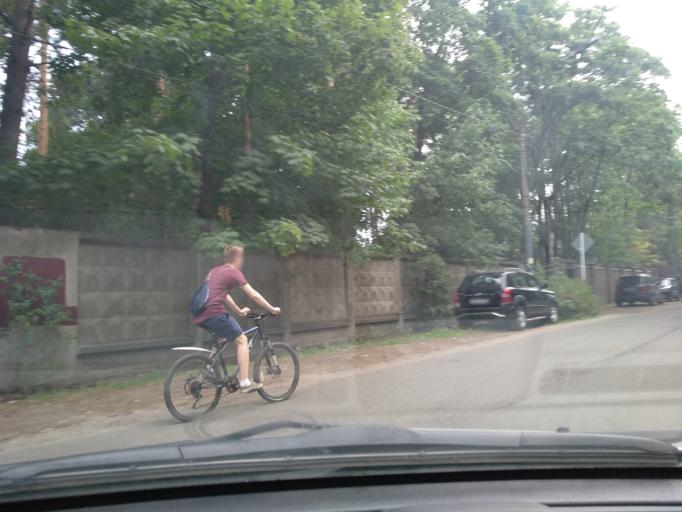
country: RU
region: Moskovskaya
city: Il'inskiy
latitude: 55.6116
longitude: 38.1024
